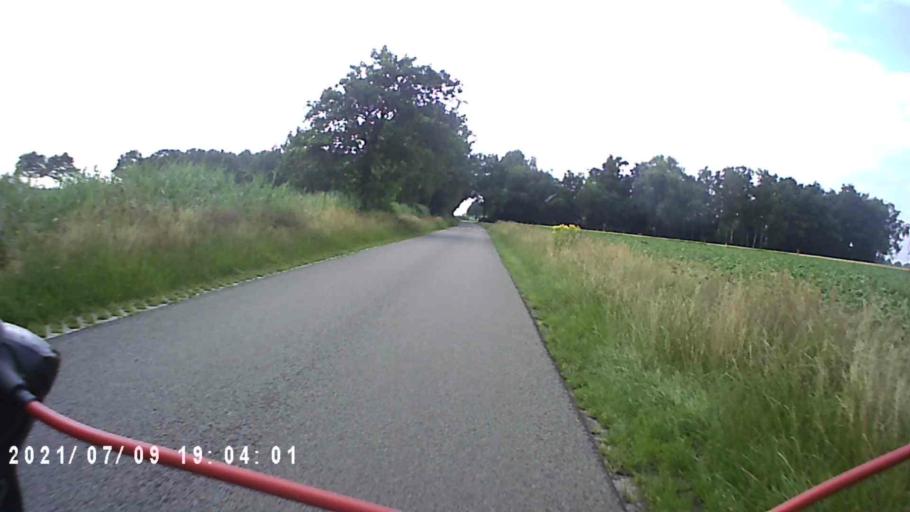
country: NL
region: Groningen
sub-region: Gemeente Veendam
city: Veendam
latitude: 53.0501
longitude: 6.8882
